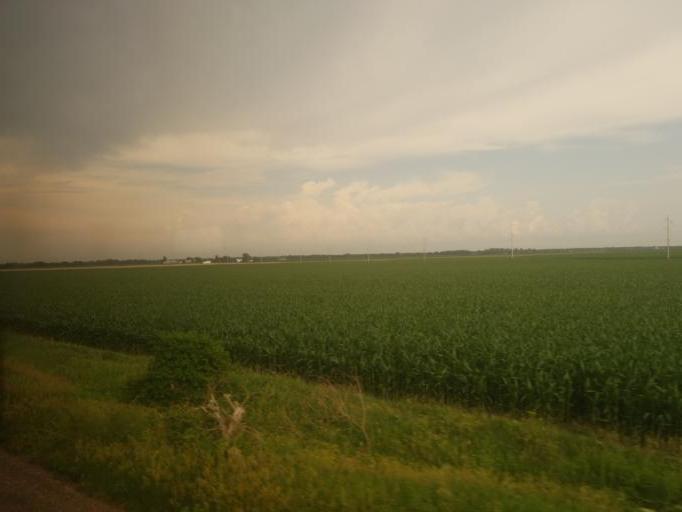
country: US
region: Illinois
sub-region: Bureau County
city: Princeton
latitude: 41.3817
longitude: -89.5354
